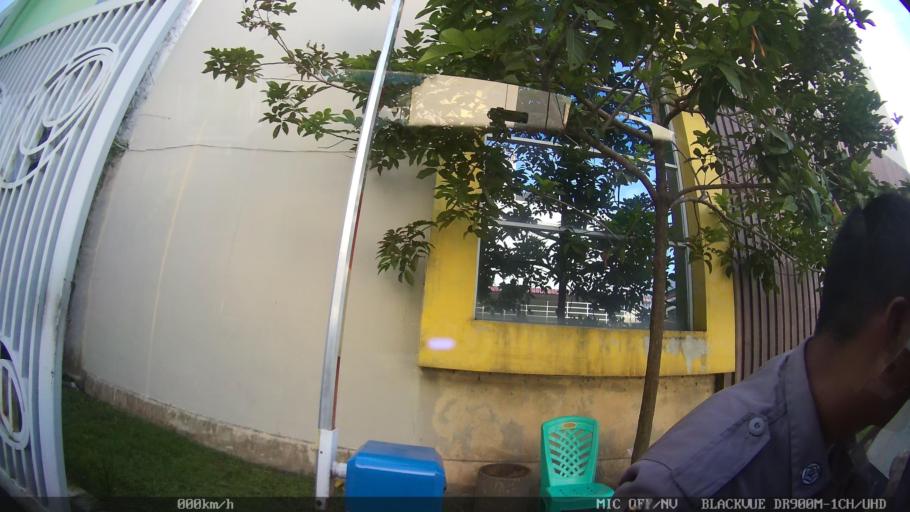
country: ID
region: North Sumatra
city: Medan
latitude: 3.6198
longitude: 98.6562
